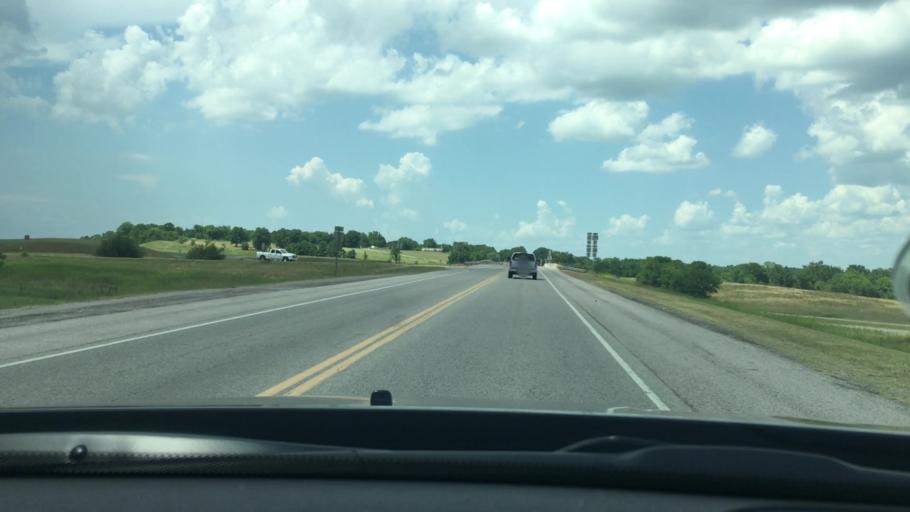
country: US
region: Oklahoma
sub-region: Pontotoc County
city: Ada
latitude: 34.7240
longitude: -96.6348
